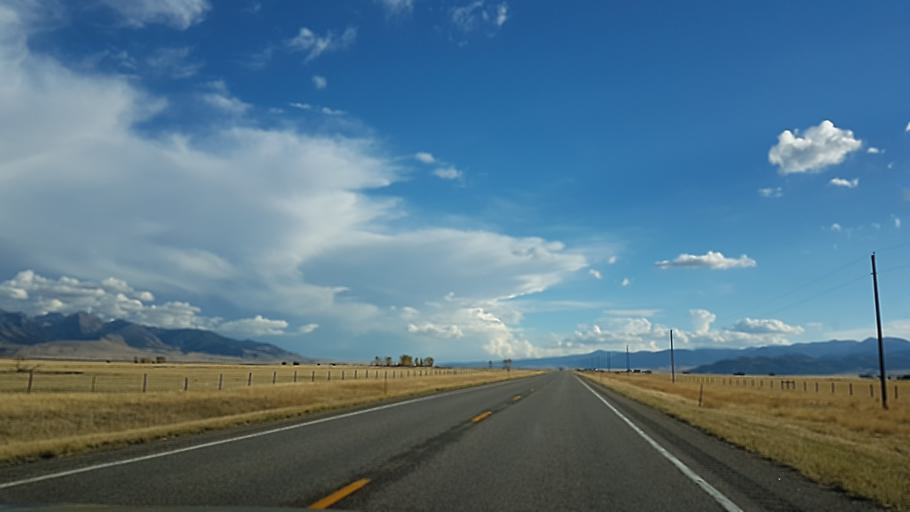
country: US
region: Montana
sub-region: Madison County
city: Virginia City
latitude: 45.1931
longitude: -111.6789
